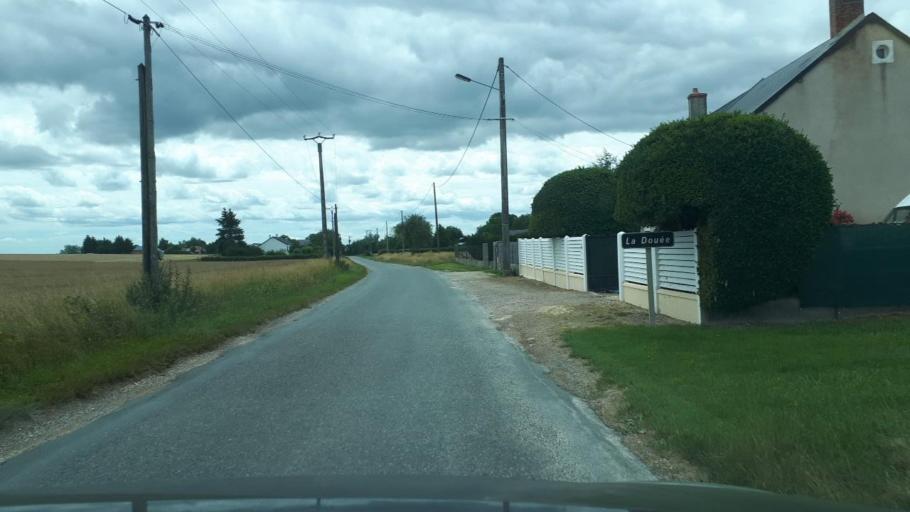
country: FR
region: Centre
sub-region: Departement du Cher
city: Rians
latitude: 47.1973
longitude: 2.6182
